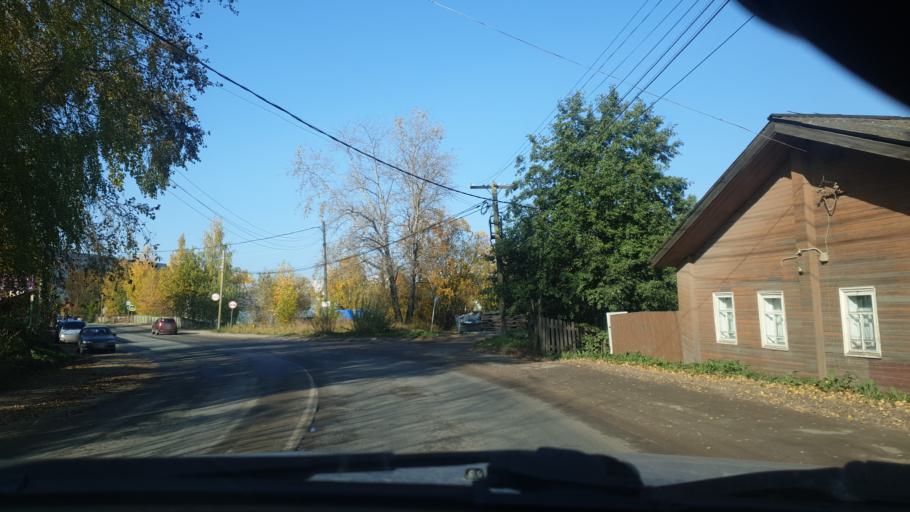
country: RU
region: Komi Republic
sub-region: Syktyvdinskiy Rayon
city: Syktyvkar
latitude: 61.6906
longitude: 50.8280
